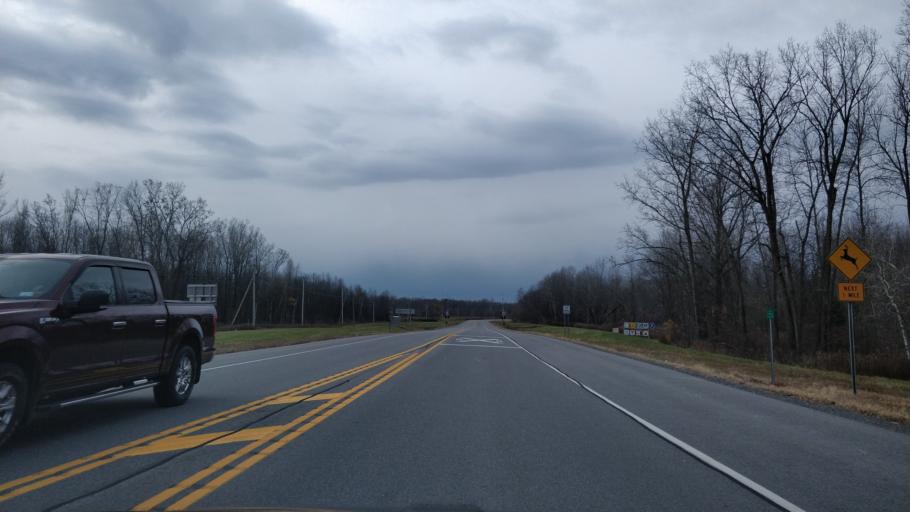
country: US
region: New York
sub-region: St. Lawrence County
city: Ogdensburg
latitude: 44.7118
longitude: -75.4506
